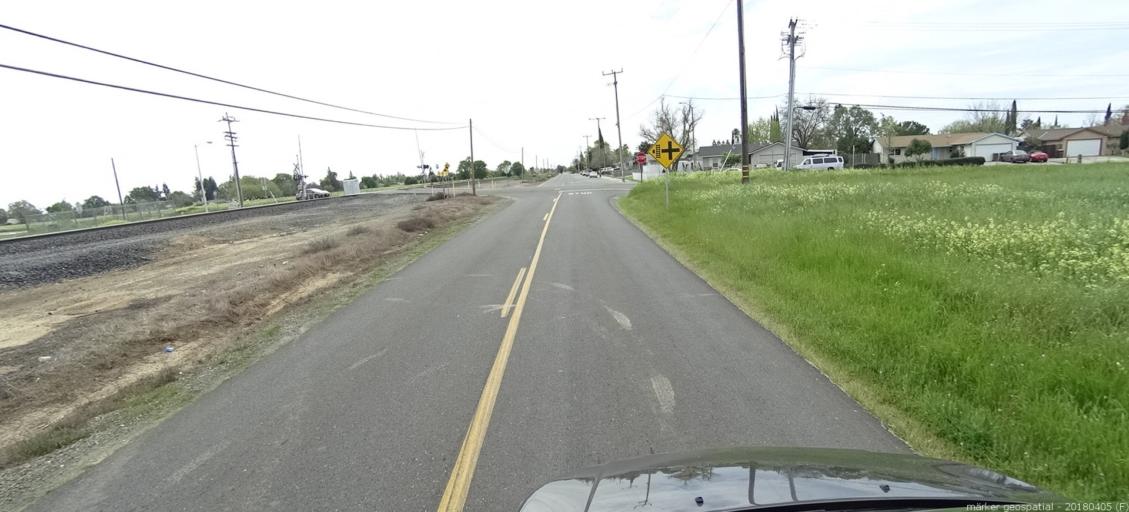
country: US
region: California
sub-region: Sacramento County
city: Galt
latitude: 38.2626
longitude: -121.3106
